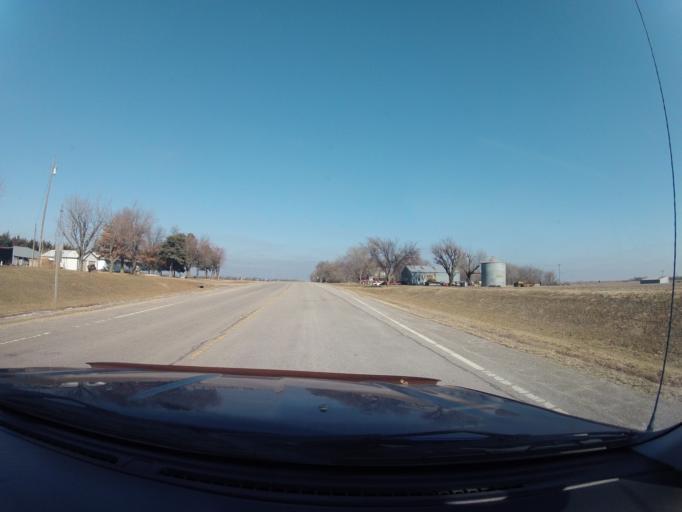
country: US
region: Kansas
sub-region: Marshall County
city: Blue Rapids
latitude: 39.5942
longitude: -96.7499
